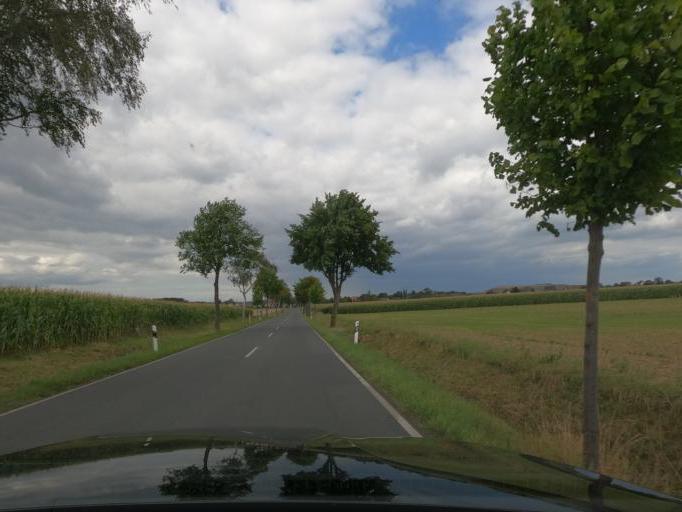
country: DE
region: Lower Saxony
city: Sehnde
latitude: 52.2867
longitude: 9.9477
